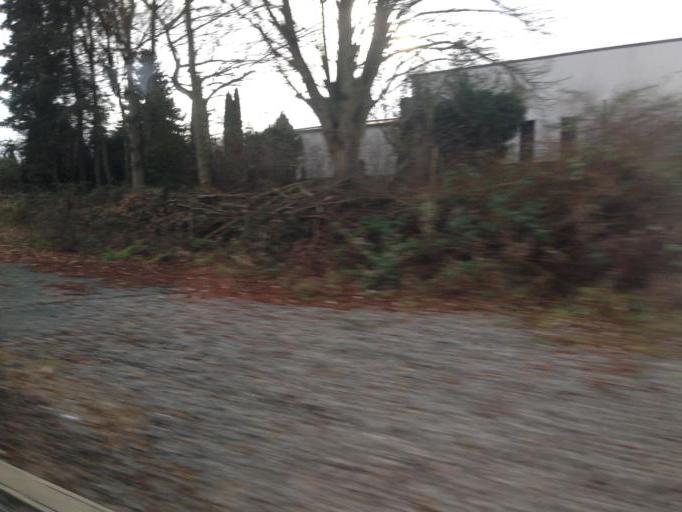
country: DE
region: Hesse
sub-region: Regierungsbezirk Giessen
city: Lich
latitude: 50.5138
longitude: 8.8242
